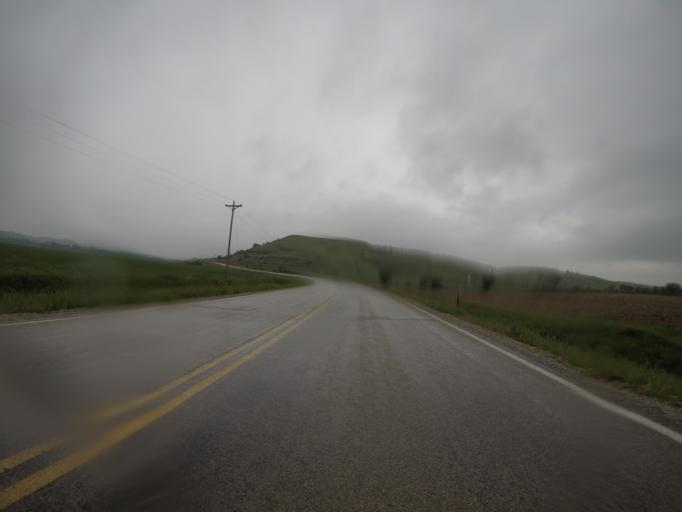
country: US
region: Kansas
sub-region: Pottawatomie County
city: Westmoreland
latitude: 39.3970
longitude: -96.1872
